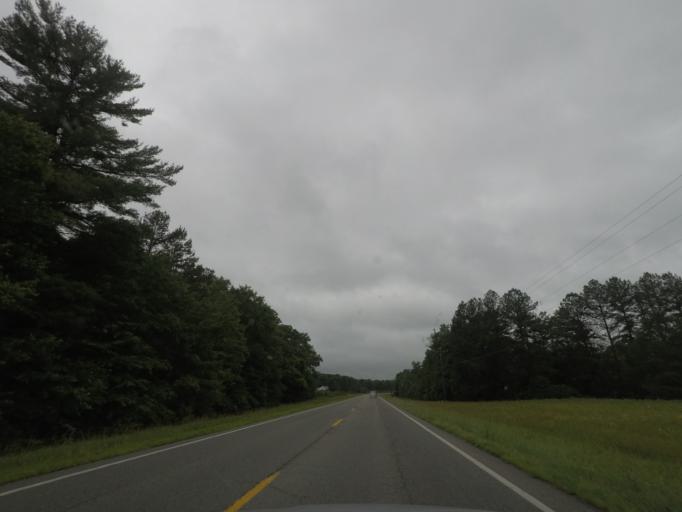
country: US
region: Virginia
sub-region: Fluvanna County
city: Palmyra
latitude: 37.8156
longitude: -78.2541
